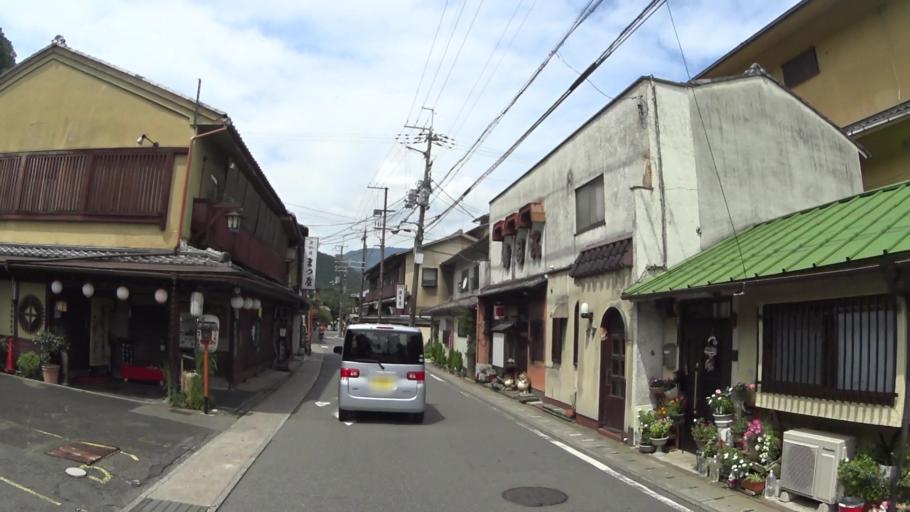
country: JP
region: Kyoto
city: Muko
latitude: 35.0106
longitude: 135.6781
